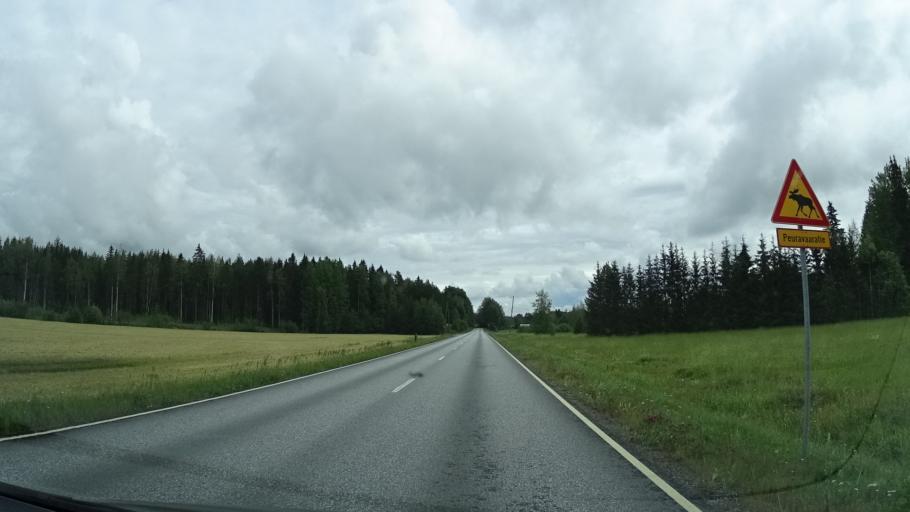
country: FI
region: Haeme
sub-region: Forssa
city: Humppila
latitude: 61.0952
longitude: 23.3626
